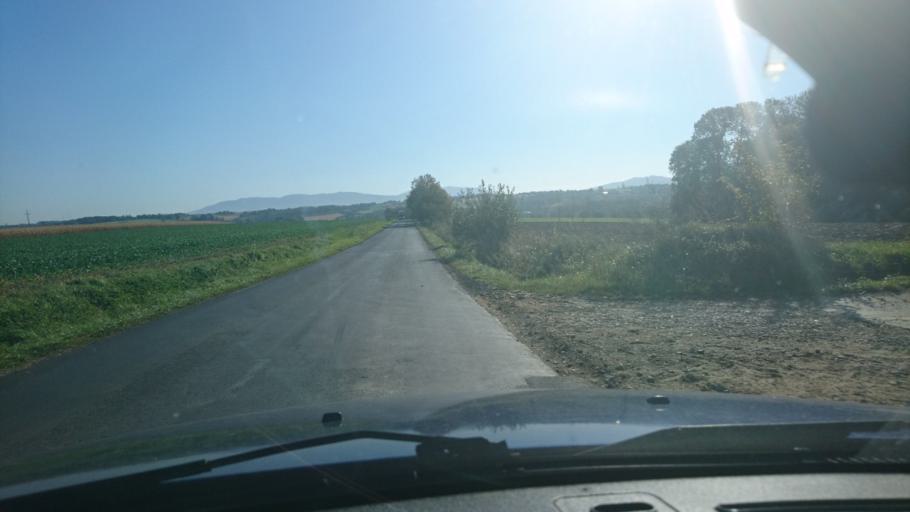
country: PL
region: Silesian Voivodeship
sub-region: Powiat bielski
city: Bronow
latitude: 49.8557
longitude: 18.9253
